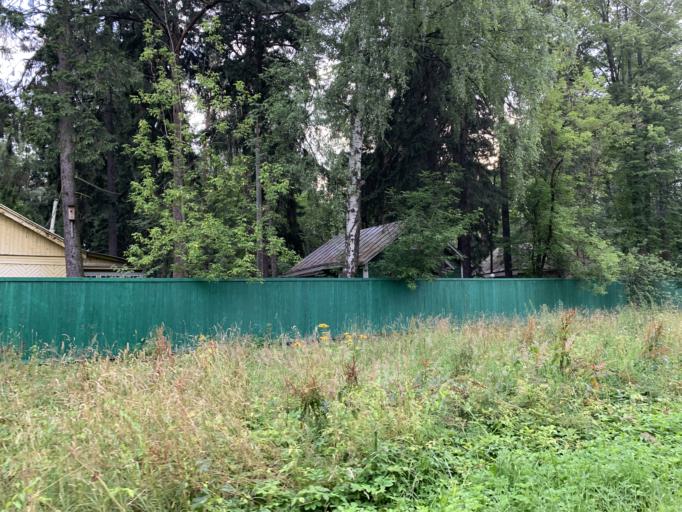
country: RU
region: Moskovskaya
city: Mamontovka
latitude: 55.9750
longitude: 37.8276
